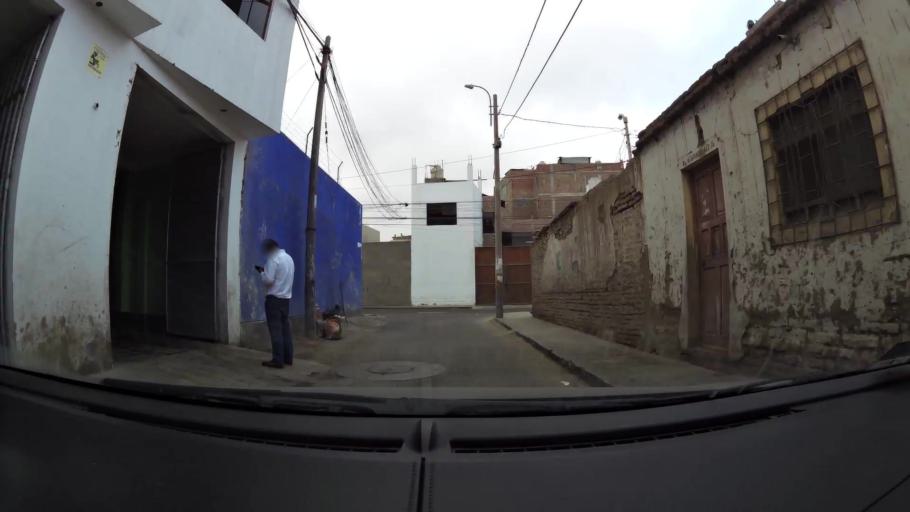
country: PE
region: La Libertad
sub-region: Provincia de Trujillo
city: Trujillo
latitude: -8.0993
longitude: -79.0246
